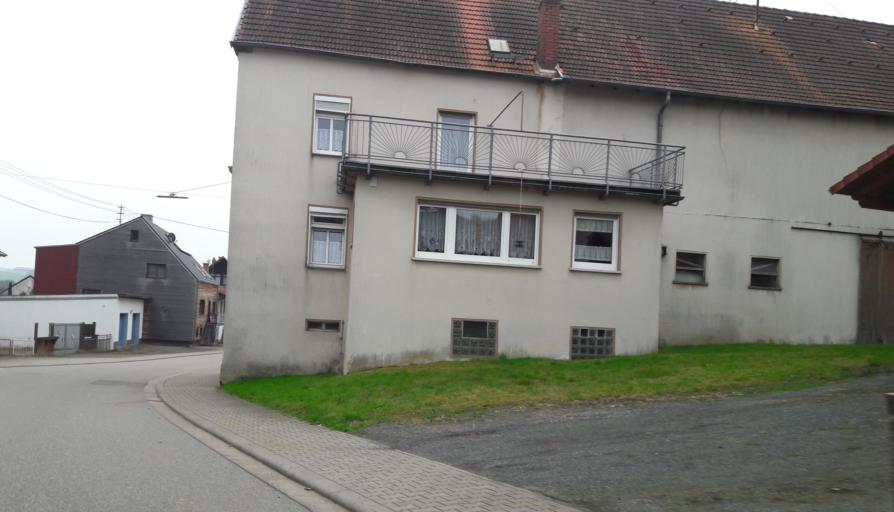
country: DE
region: Rheinland-Pfalz
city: Langenbach
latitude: 49.4951
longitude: 7.3219
